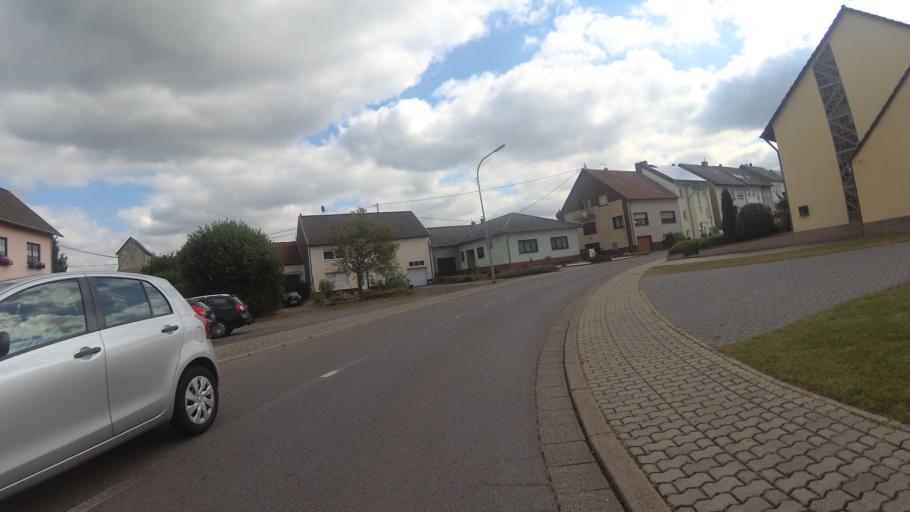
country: DE
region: Saarland
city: Wadgassen
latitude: 49.2423
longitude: 6.7507
